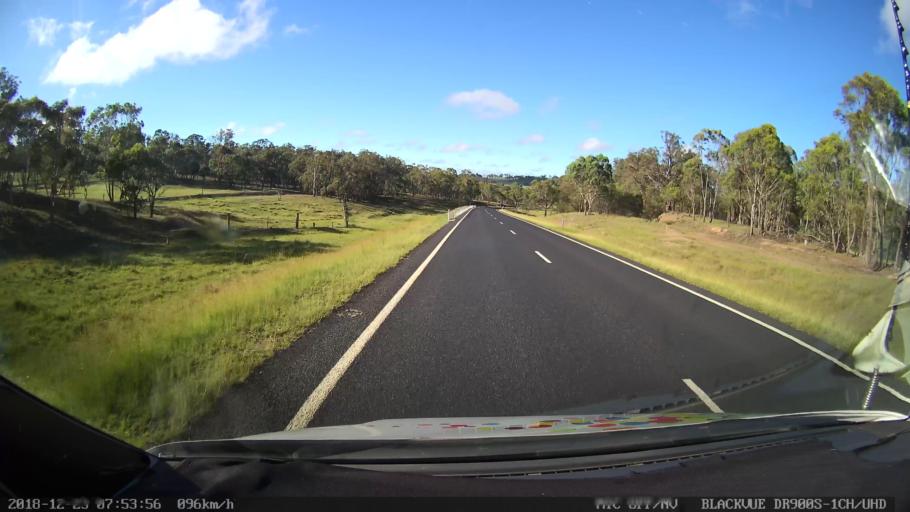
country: AU
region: New South Wales
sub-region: Armidale Dumaresq
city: Armidale
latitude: -30.5408
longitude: 151.8030
